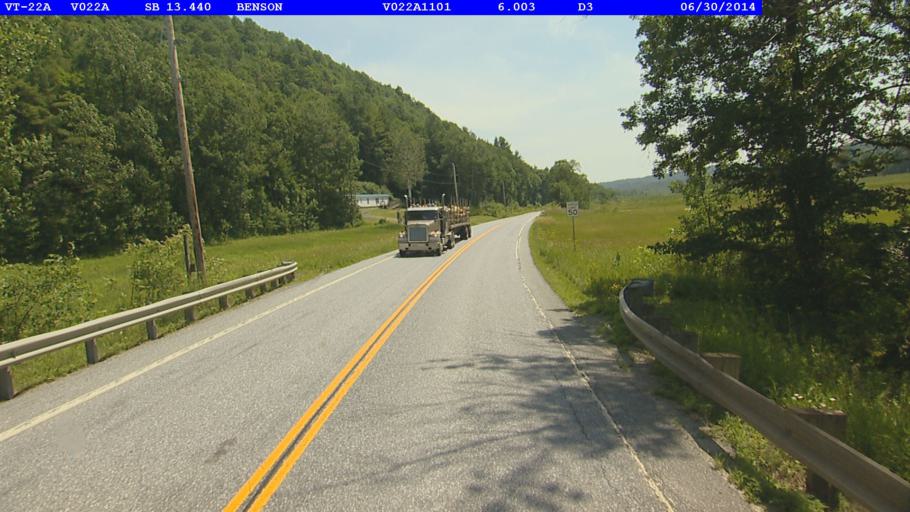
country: US
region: New York
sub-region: Essex County
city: Ticonderoga
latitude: 43.7539
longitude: -73.3092
